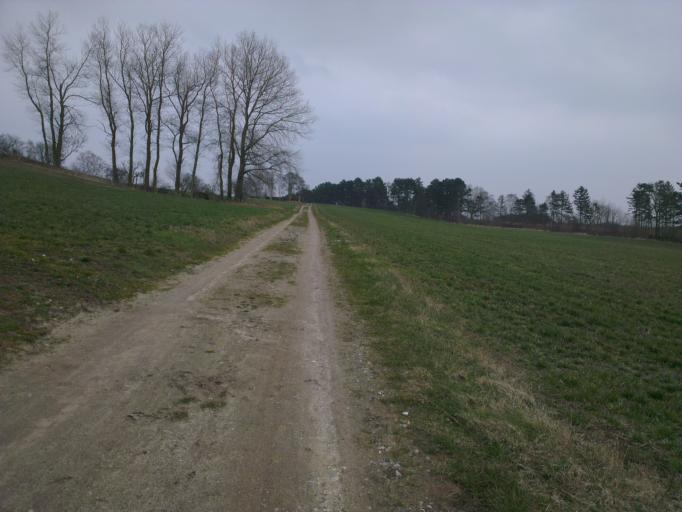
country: DK
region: Capital Region
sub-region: Frederikssund Kommune
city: Frederikssund
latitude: 55.8264
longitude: 12.0238
